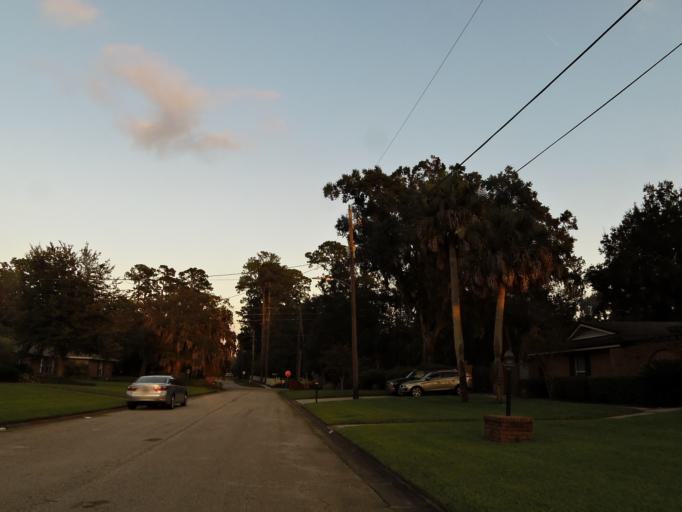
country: US
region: Florida
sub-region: Clay County
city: Orange Park
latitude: 30.1903
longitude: -81.6321
